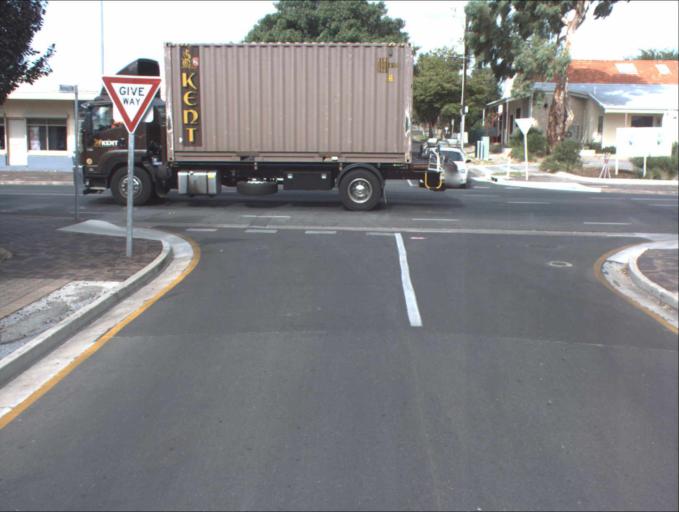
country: AU
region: South Australia
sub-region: Port Adelaide Enfield
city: Blair Athol
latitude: -34.8672
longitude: 138.5924
